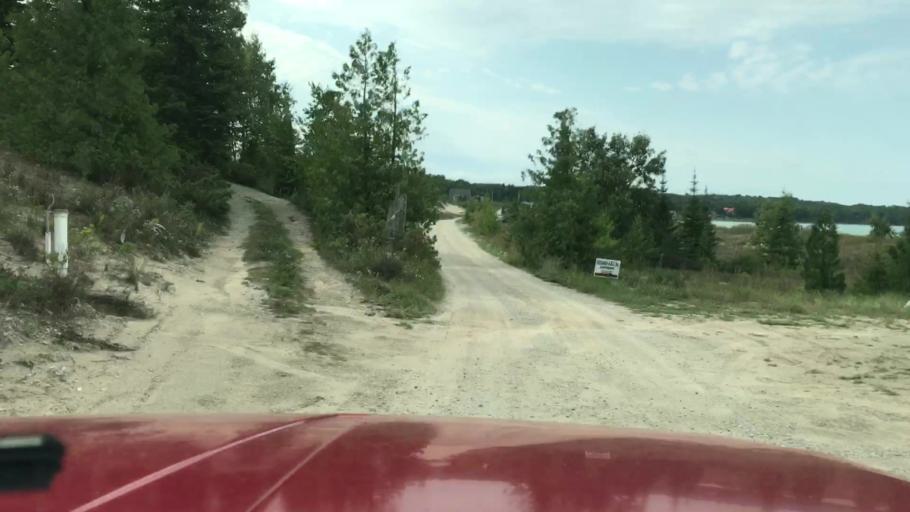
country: US
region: Michigan
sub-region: Charlevoix County
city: Charlevoix
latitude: 45.7415
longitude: -85.5613
